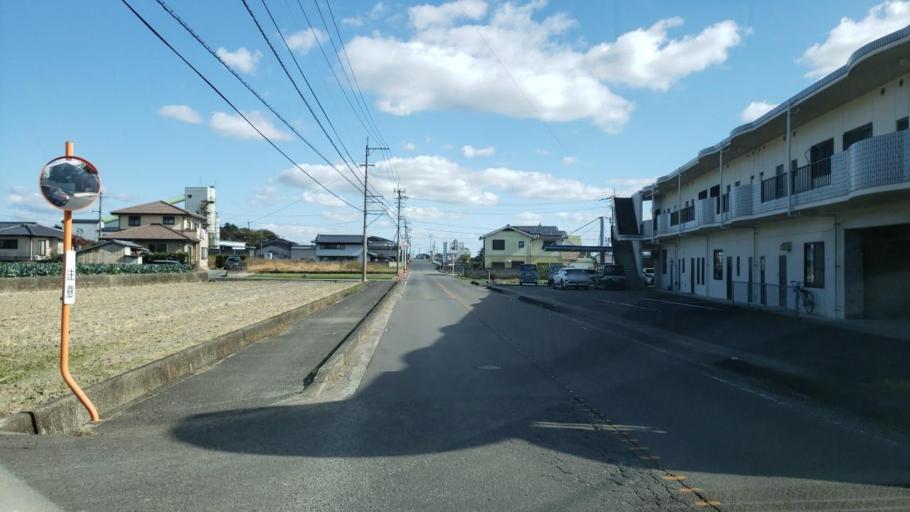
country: JP
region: Tokushima
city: Wakimachi
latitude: 34.0821
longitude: 134.2201
